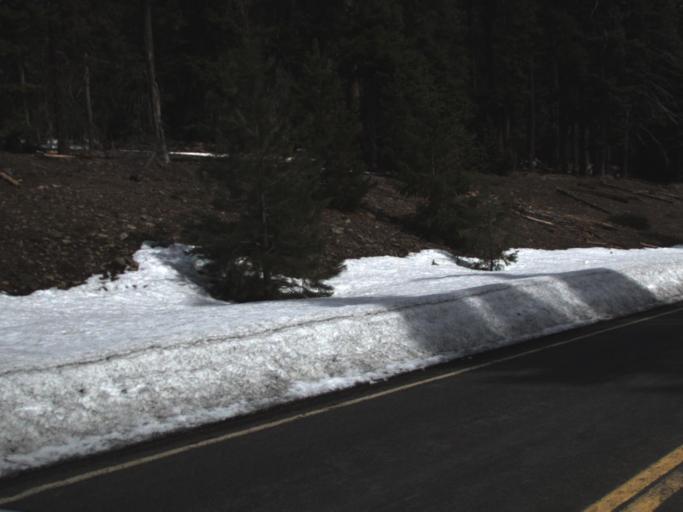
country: US
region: Washington
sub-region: Kittitas County
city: Cle Elum
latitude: 46.9666
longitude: -121.2512
